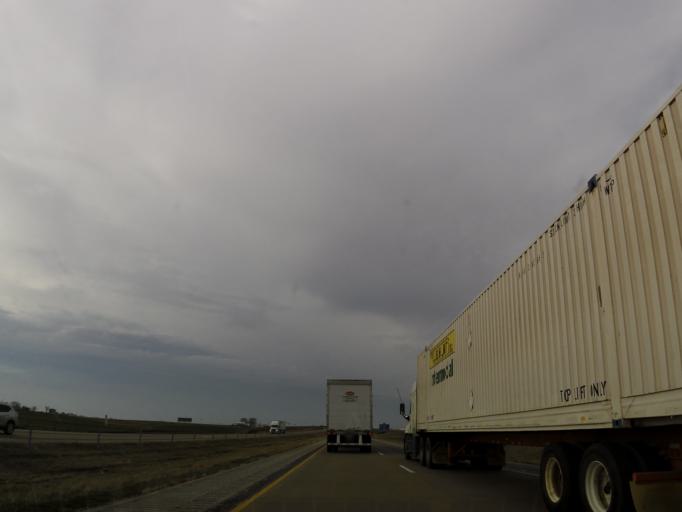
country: US
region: Iowa
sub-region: Scott County
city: Walcott
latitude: 41.6063
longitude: -90.7328
